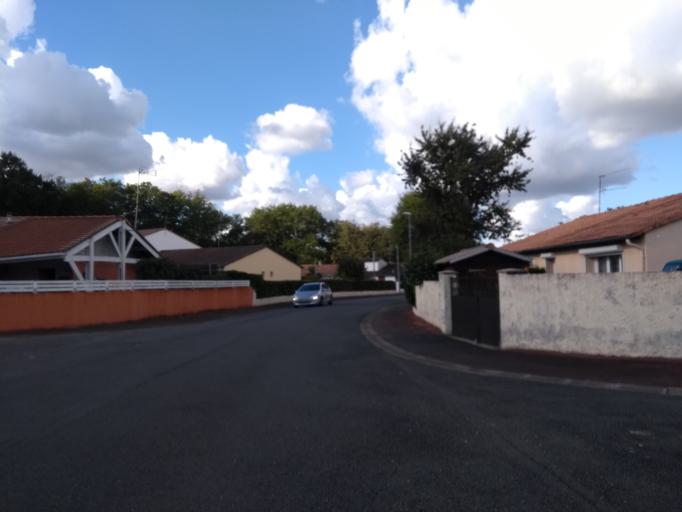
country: FR
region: Aquitaine
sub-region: Departement de la Gironde
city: Canejan
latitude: 44.7570
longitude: -0.6424
